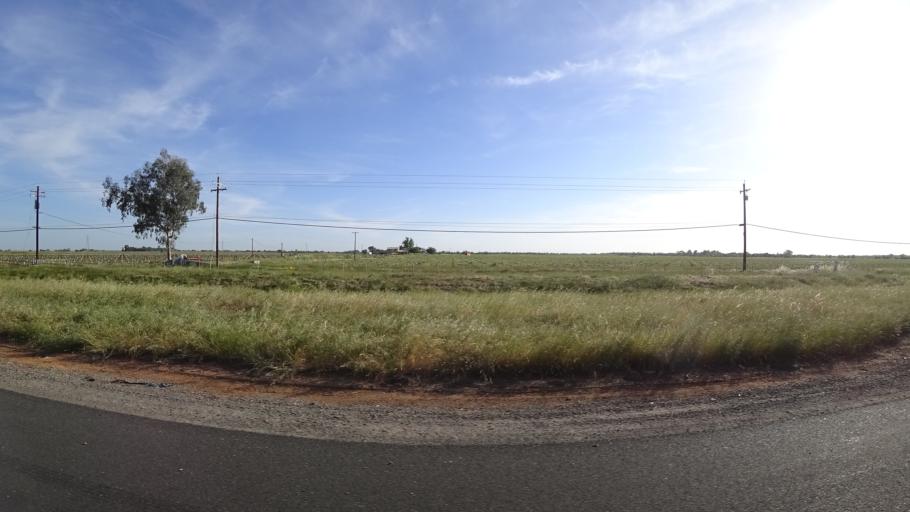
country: US
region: California
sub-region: Placer County
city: Sheridan
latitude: 38.9905
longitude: -121.3903
